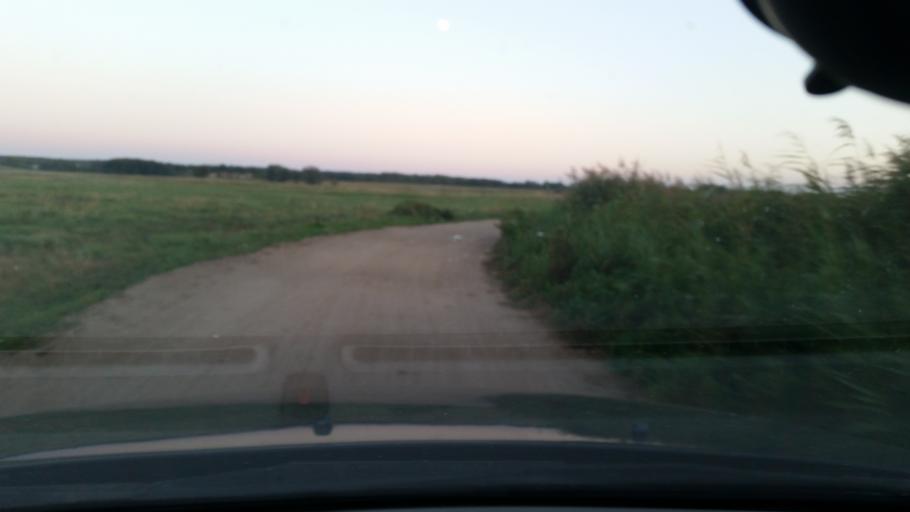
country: PL
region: Pomeranian Voivodeship
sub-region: Powiat wejherowski
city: Choczewo
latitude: 54.7874
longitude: 17.7948
